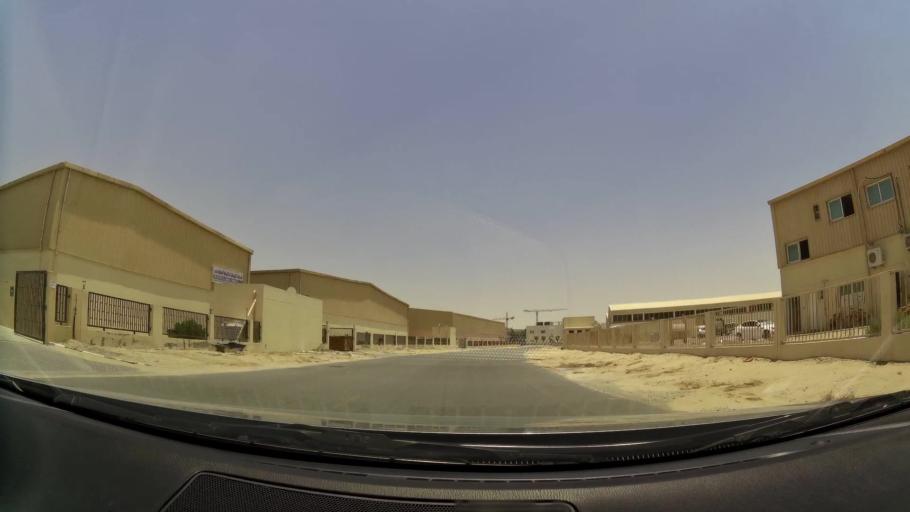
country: AE
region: Dubai
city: Dubai
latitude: 24.9856
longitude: 55.1718
